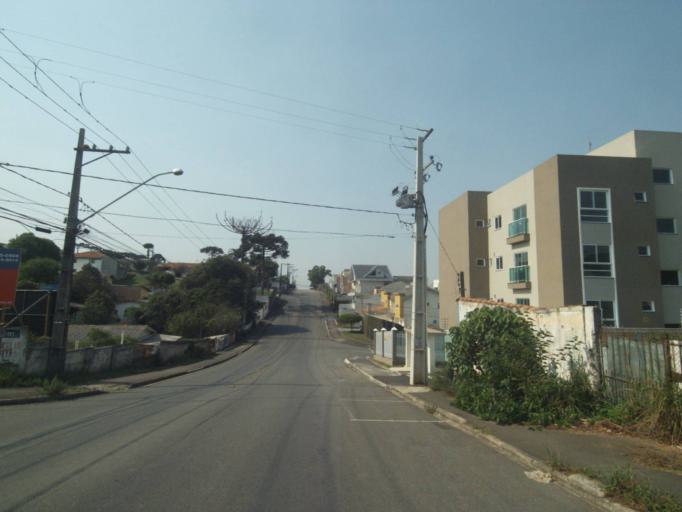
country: BR
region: Parana
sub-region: Sao Jose Dos Pinhais
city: Sao Jose dos Pinhais
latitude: -25.5186
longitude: -49.2491
